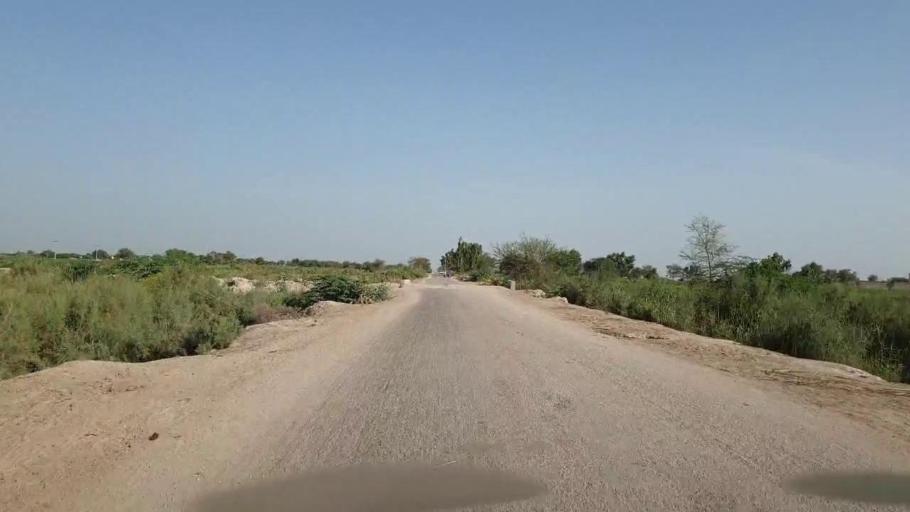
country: PK
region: Sindh
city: Nawabshah
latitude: 26.1647
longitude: 68.4424
